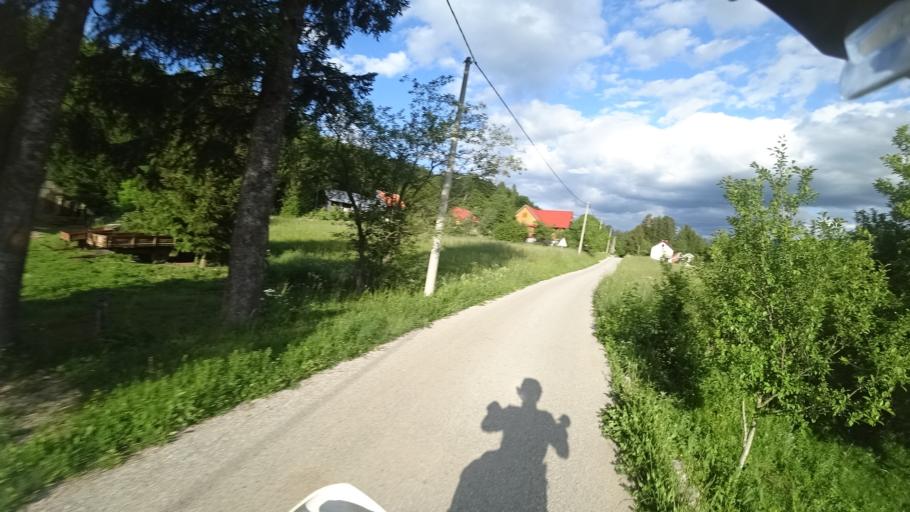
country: HR
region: Licko-Senjska
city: Gospic
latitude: 44.4911
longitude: 15.3077
